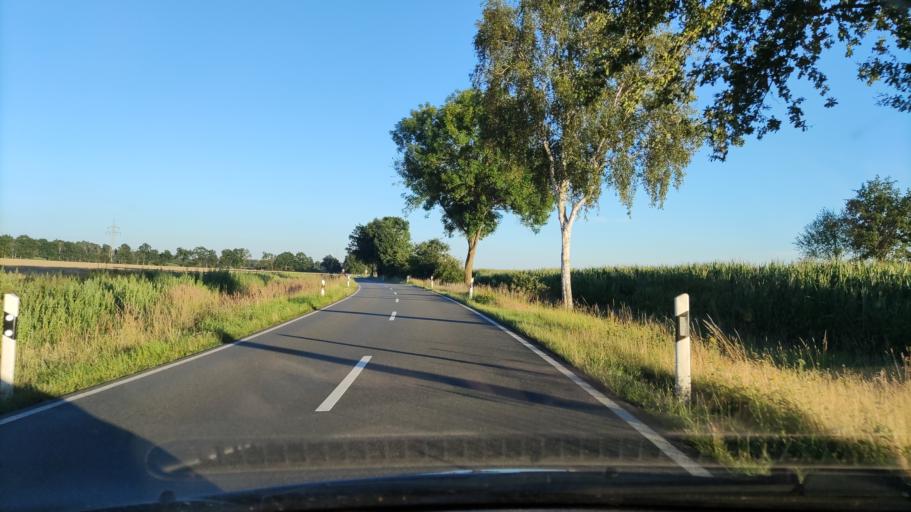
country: DE
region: Lower Saxony
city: Luechow
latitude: 53.0144
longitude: 11.1506
